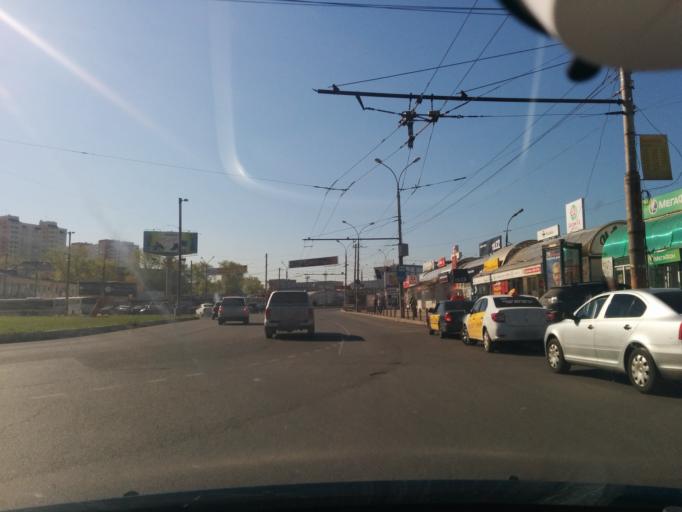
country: RU
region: Perm
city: Perm
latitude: 58.0036
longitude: 56.2305
